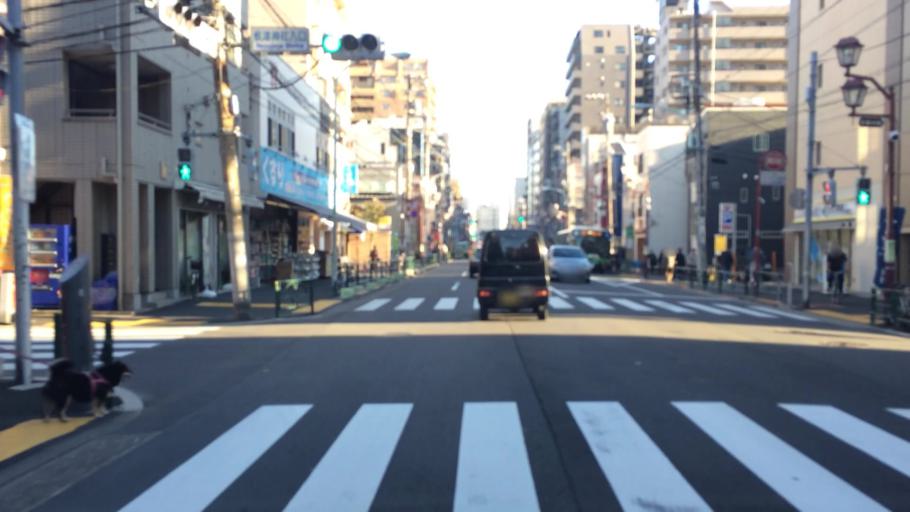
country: JP
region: Tokyo
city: Tokyo
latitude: 35.7201
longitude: 139.7630
